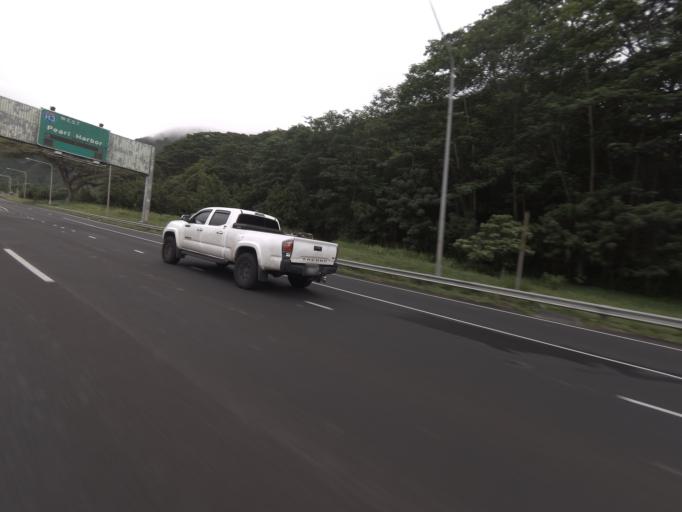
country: US
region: Hawaii
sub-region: Honolulu County
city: Kane'ohe
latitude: 21.3980
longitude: -157.8104
